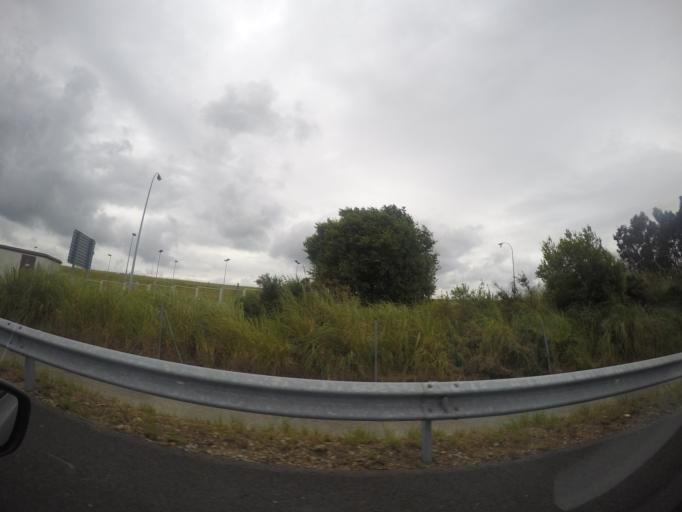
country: ES
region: Galicia
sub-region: Provincia da Coruna
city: Culleredo
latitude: 43.3064
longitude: -8.3770
